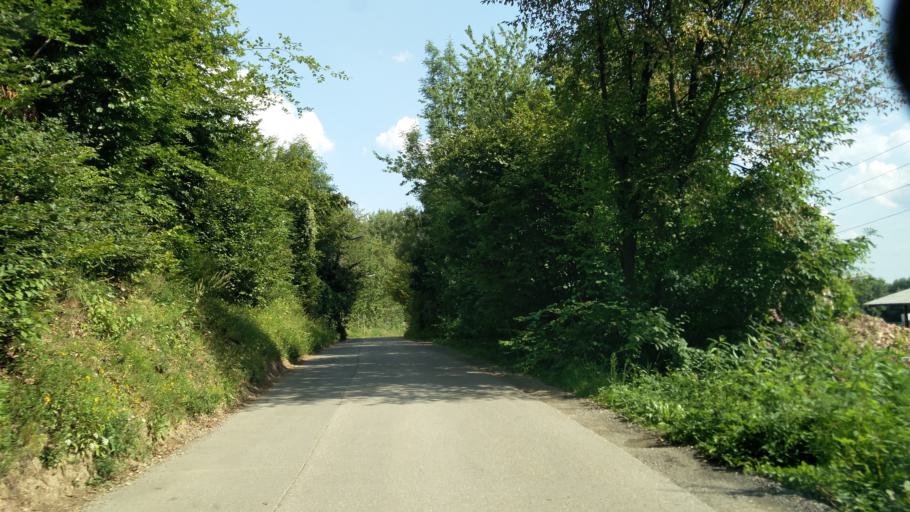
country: AT
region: Styria
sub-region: Politischer Bezirk Weiz
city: Weiz
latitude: 47.2303
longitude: 15.6169
